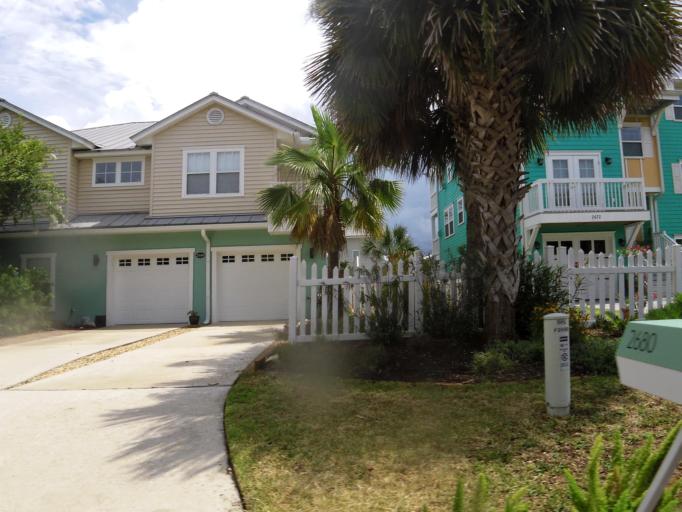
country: US
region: Florida
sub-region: Nassau County
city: Fernandina Beach
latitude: 30.6773
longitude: -81.4327
